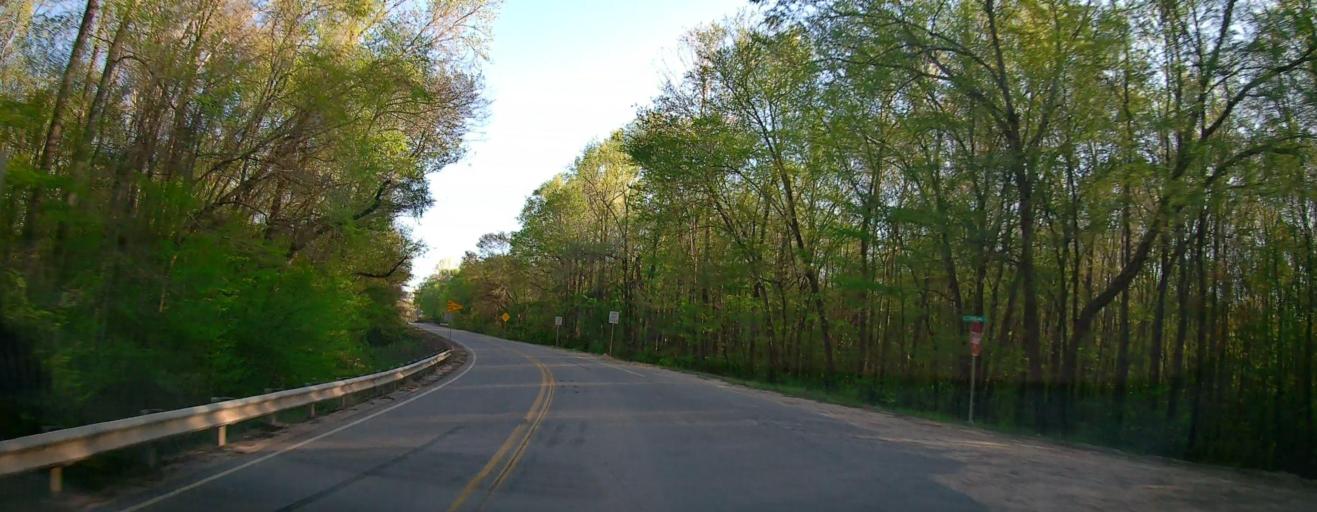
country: US
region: Georgia
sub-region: Wilkinson County
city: Irwinton
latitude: 32.8336
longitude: -83.0796
